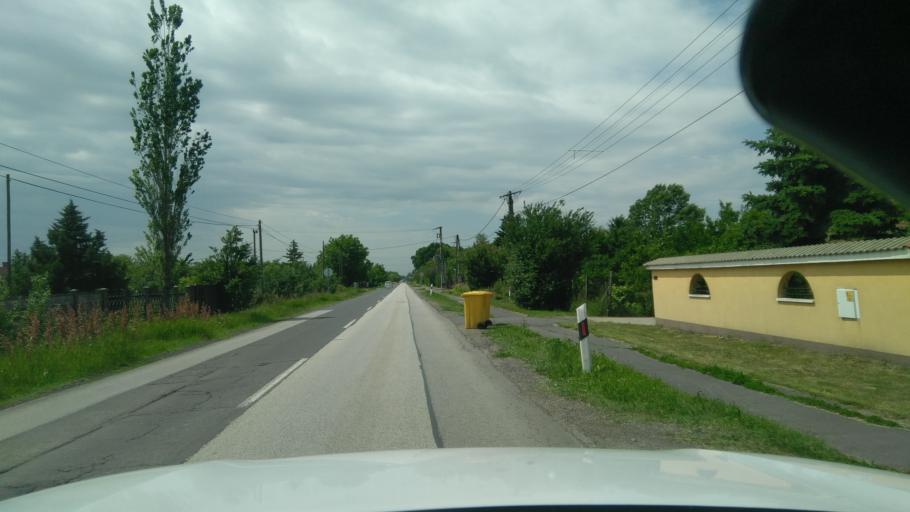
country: HU
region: Bekes
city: Bekescsaba
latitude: 46.6993
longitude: 21.1407
